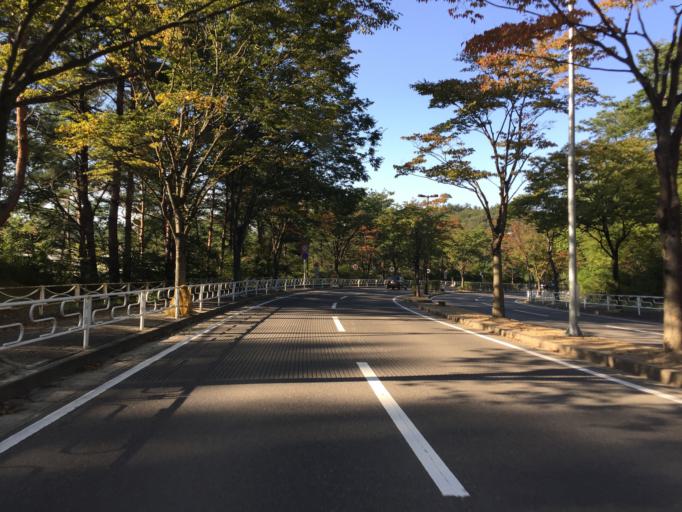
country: JP
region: Fukushima
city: Fukushima-shi
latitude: 37.7006
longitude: 140.4708
